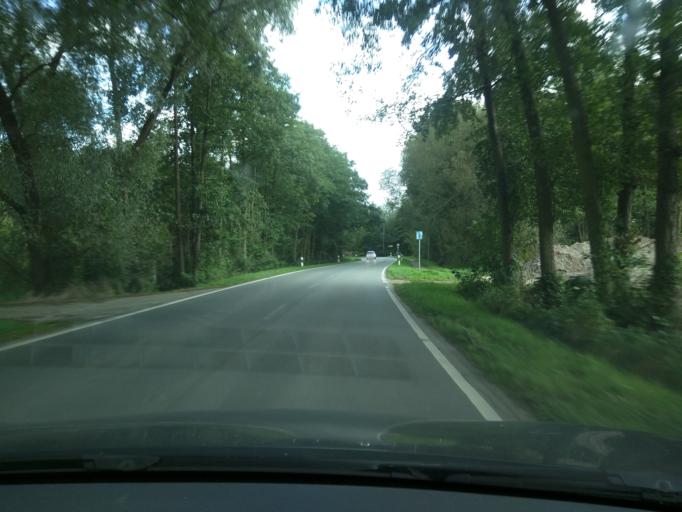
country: DE
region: Lower Saxony
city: Tespe
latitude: 53.3919
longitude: 10.4274
